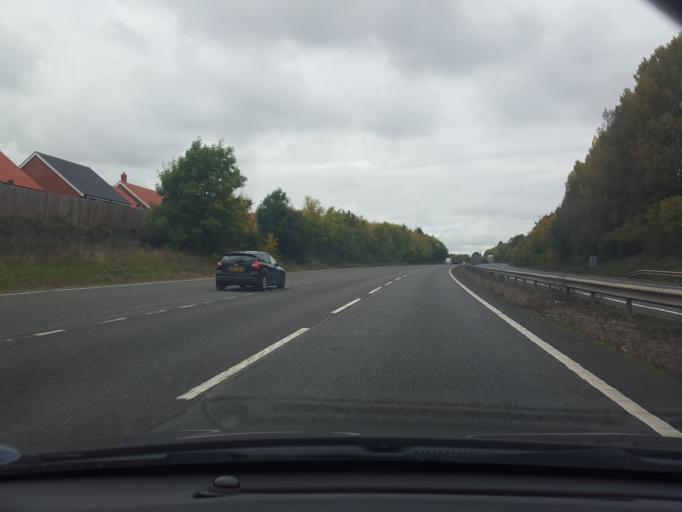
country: GB
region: England
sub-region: Suffolk
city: Stowmarket
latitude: 52.1897
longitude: 1.0177
